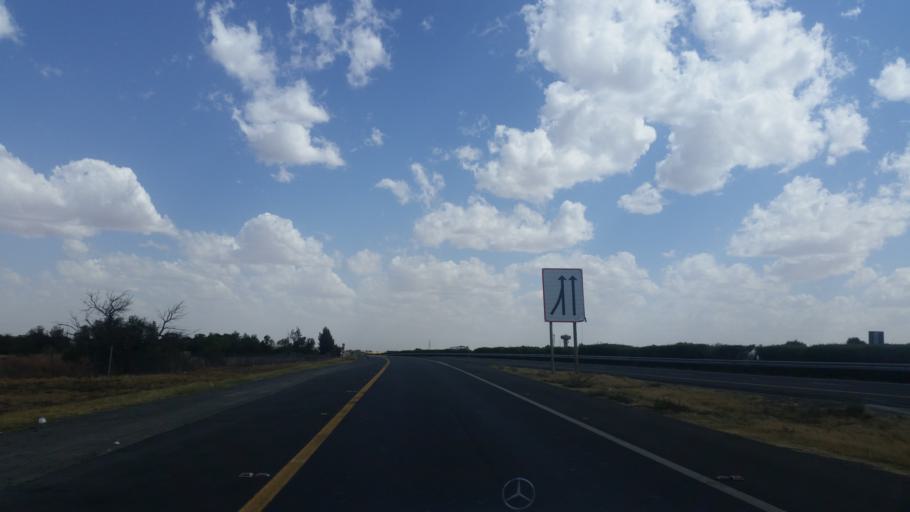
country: ZA
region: Orange Free State
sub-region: Mangaung Metropolitan Municipality
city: Bloemfontein
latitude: -29.0761
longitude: 26.1815
